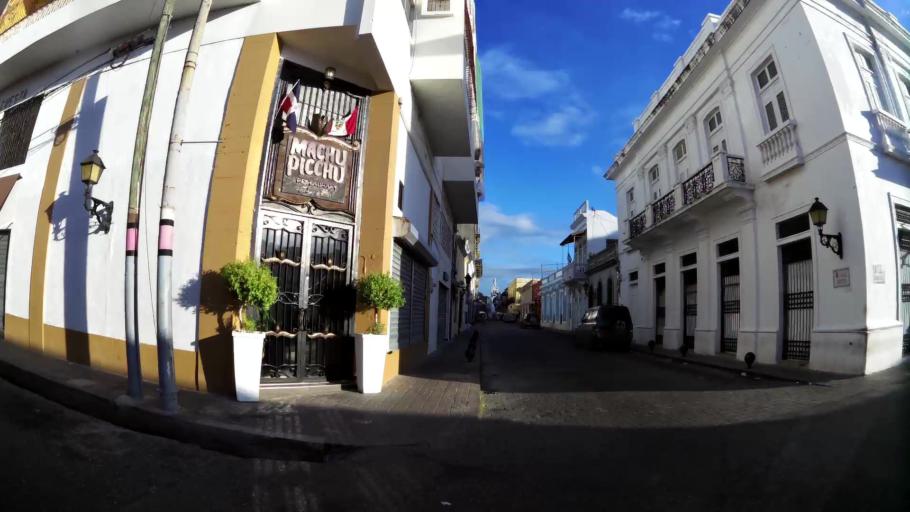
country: DO
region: Nacional
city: Ciudad Nueva
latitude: 18.4726
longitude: -69.8852
